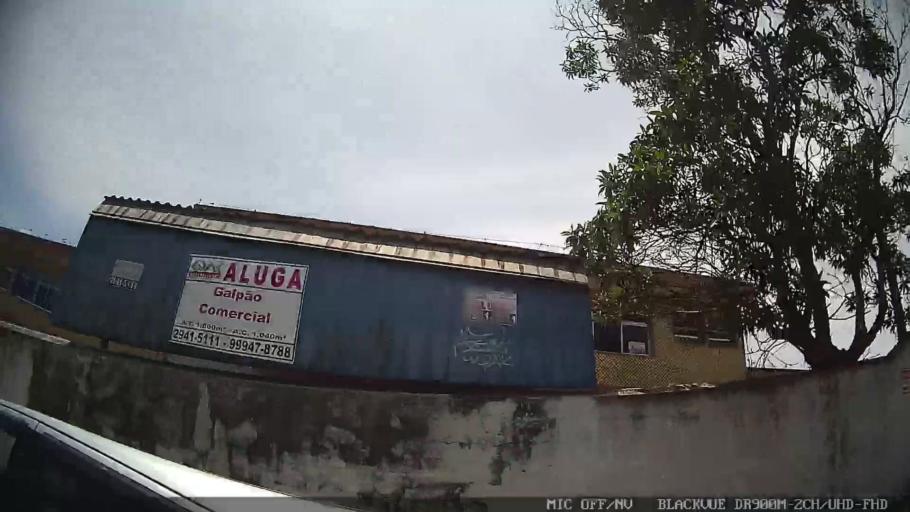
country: BR
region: Sao Paulo
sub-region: Sao Caetano Do Sul
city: Sao Caetano do Sul
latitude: -23.5703
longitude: -46.5559
